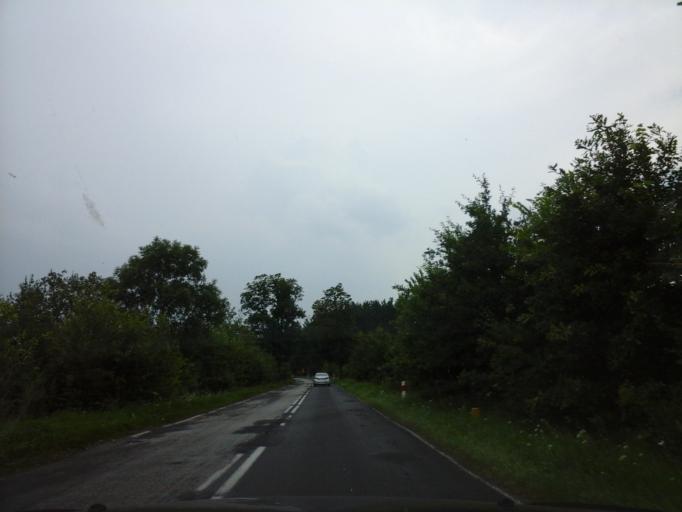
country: PL
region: Lubusz
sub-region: Powiat strzelecko-drezdenecki
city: Drezdenko
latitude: 52.8155
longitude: 15.8276
